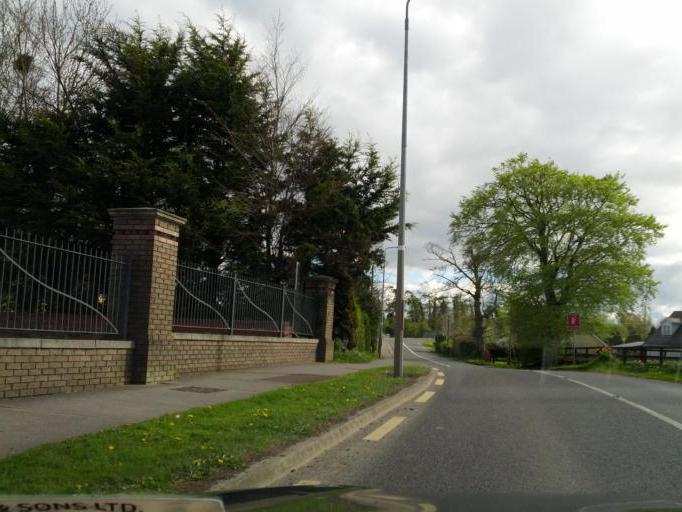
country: IE
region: Leinster
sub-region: Kildare
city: Kilcock
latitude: 53.4068
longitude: -6.6781
